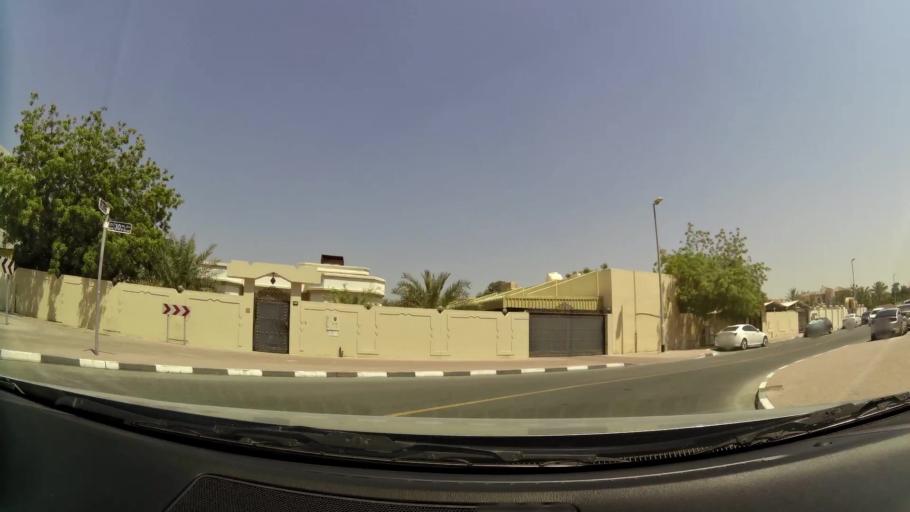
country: AE
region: Dubai
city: Dubai
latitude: 25.2111
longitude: 55.2691
